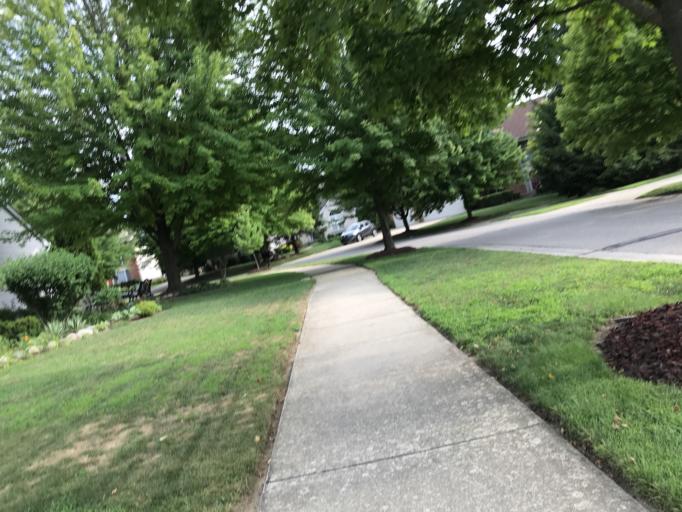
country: US
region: Michigan
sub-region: Oakland County
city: Franklin
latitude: 42.4979
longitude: -83.3362
